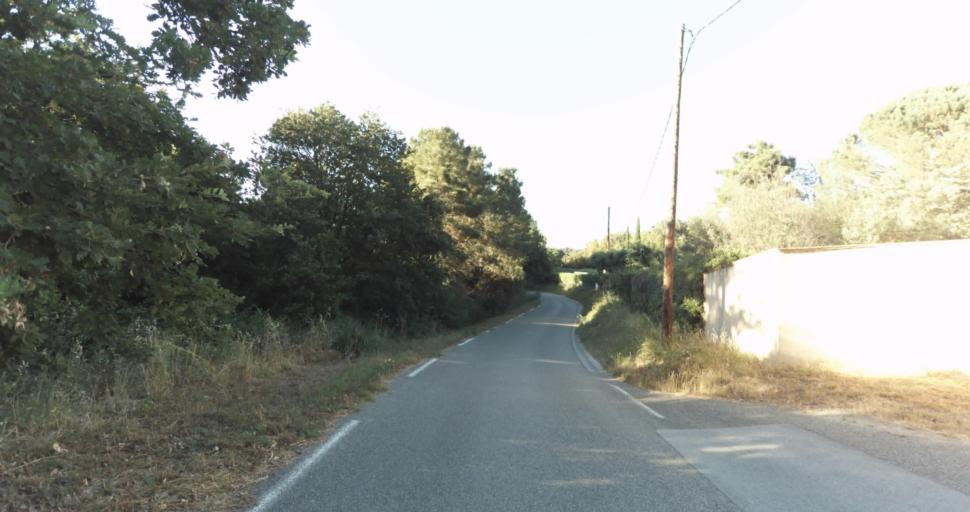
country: FR
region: Provence-Alpes-Cote d'Azur
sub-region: Departement du Var
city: Gassin
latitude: 43.2286
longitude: 6.5934
